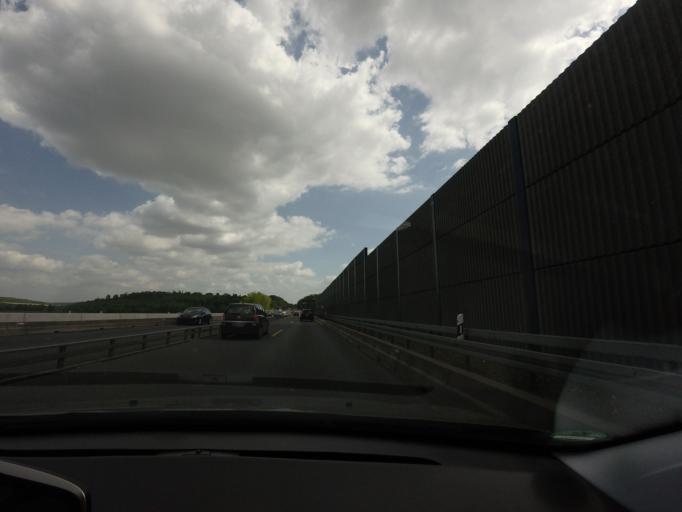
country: DE
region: Lower Saxony
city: Holle
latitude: 52.0992
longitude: 10.1539
